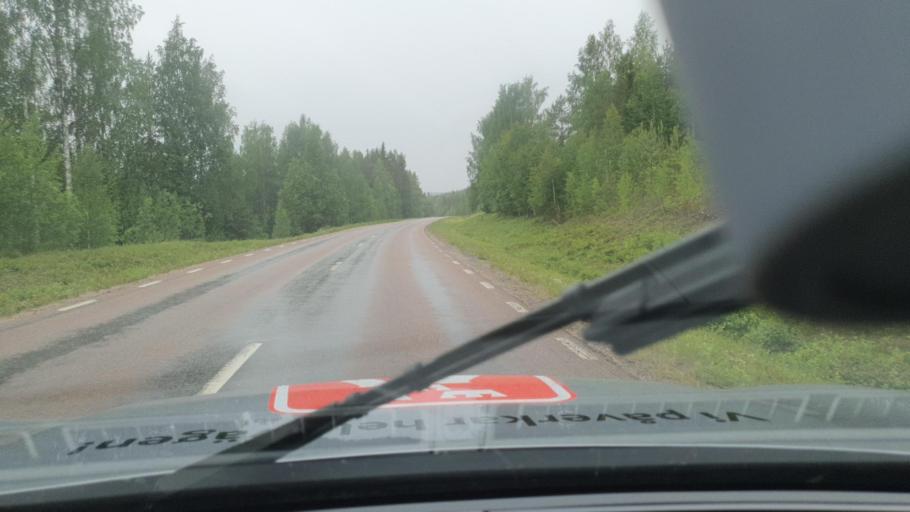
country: SE
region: Norrbotten
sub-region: Overtornea Kommun
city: OEvertornea
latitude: 66.4296
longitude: 23.3393
